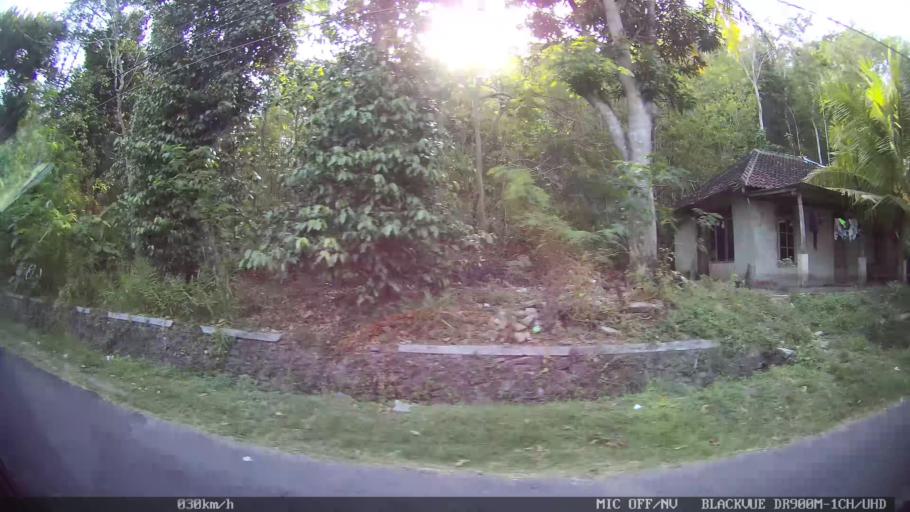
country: ID
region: Daerah Istimewa Yogyakarta
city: Bantul
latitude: -7.8763
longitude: 110.3150
